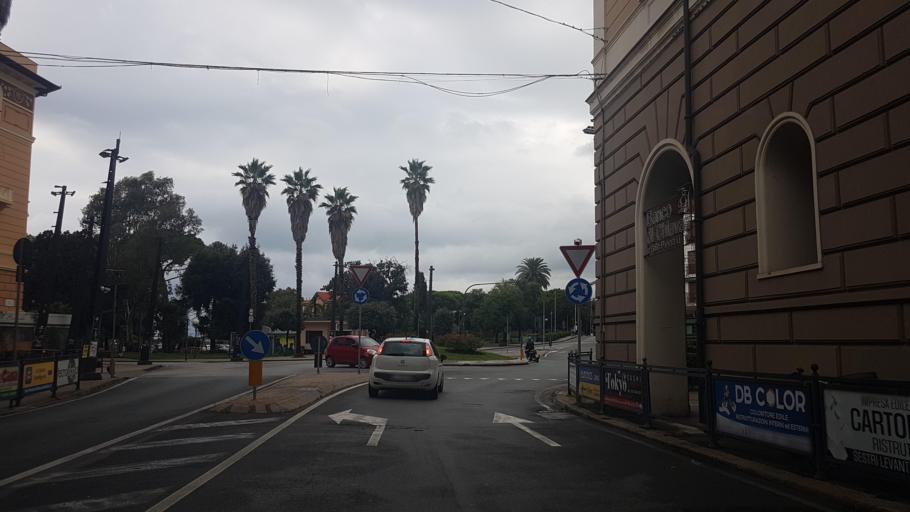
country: IT
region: Liguria
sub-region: Provincia di Genova
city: Sestri Levante
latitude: 44.2728
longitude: 9.3974
